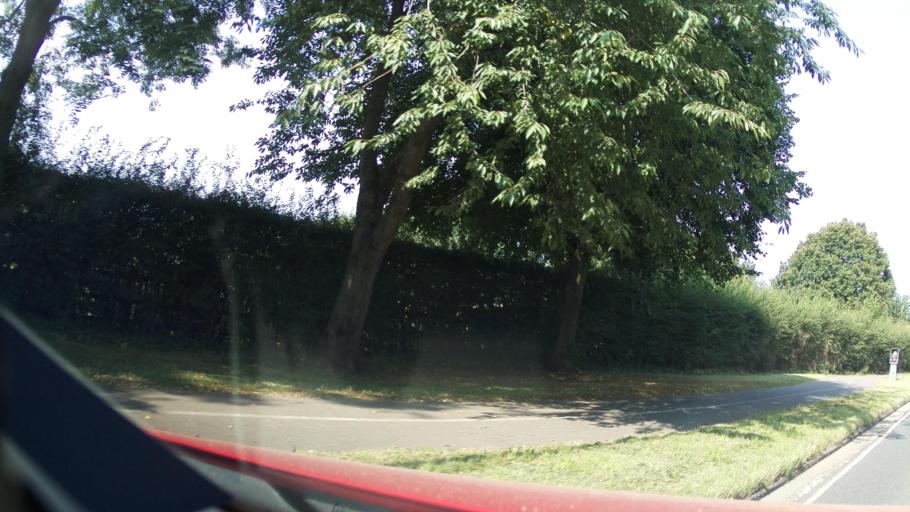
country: GB
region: England
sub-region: Derby
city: Derby
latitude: 52.9396
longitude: -1.5034
